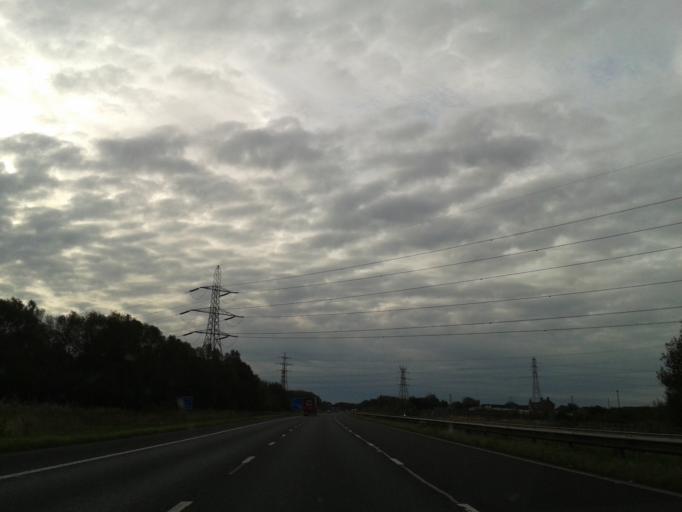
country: GB
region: England
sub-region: Cumbria
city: Carlisle
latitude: 54.9454
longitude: -2.9716
